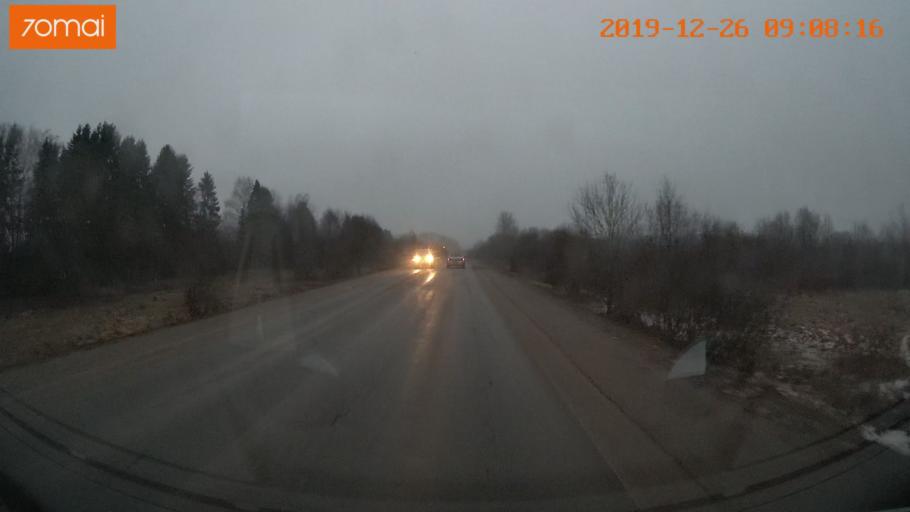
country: RU
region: Vologda
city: Gryazovets
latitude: 58.8548
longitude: 40.2479
